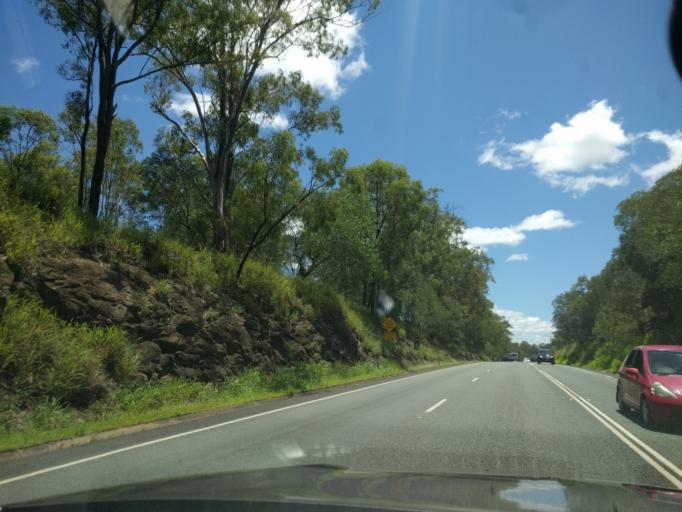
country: AU
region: Queensland
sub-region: Logan
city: Cedar Vale
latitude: -27.8409
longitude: 153.0240
